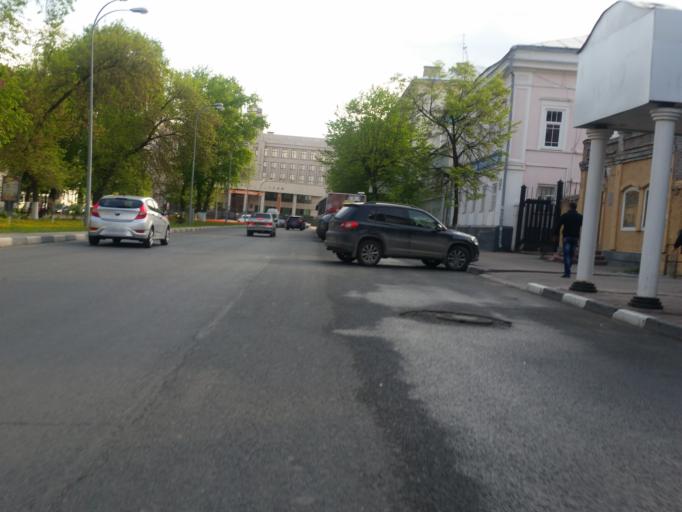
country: RU
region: Ulyanovsk
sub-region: Ulyanovskiy Rayon
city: Ulyanovsk
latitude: 54.3207
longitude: 48.4007
